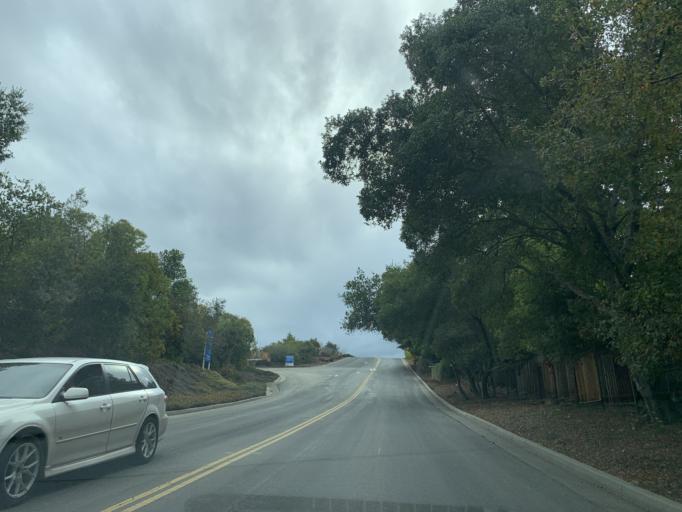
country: US
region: California
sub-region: Santa Clara County
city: Monte Sereno
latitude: 37.2581
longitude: -121.9846
